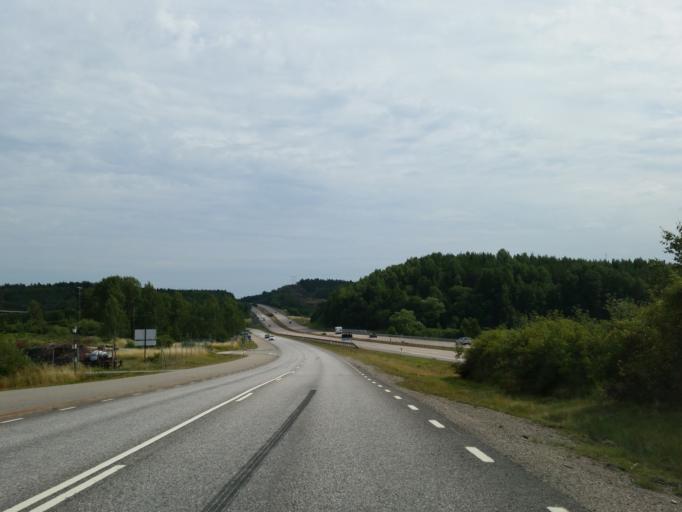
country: SE
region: Soedermanland
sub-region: Strangnas Kommun
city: Mariefred
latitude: 59.2462
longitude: 17.1689
